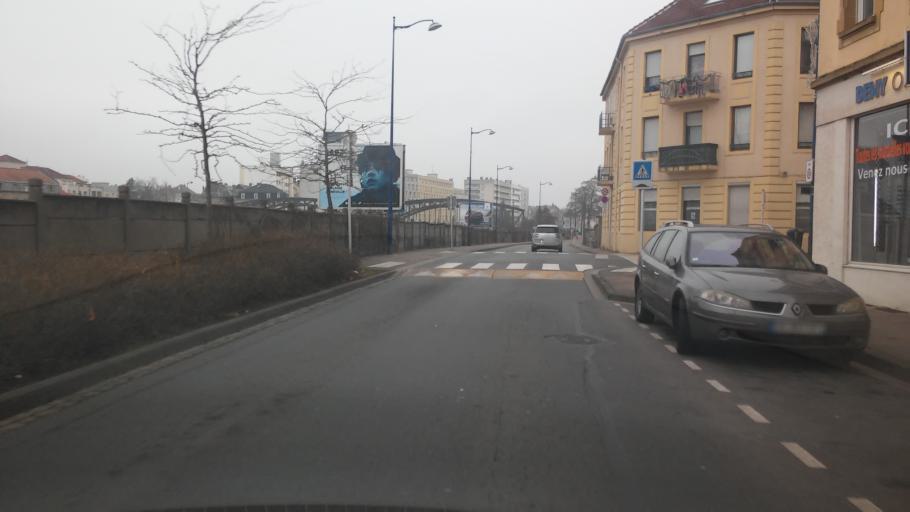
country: FR
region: Lorraine
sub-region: Departement de la Moselle
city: Montigny-les-Metz
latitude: 49.1000
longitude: 6.1688
